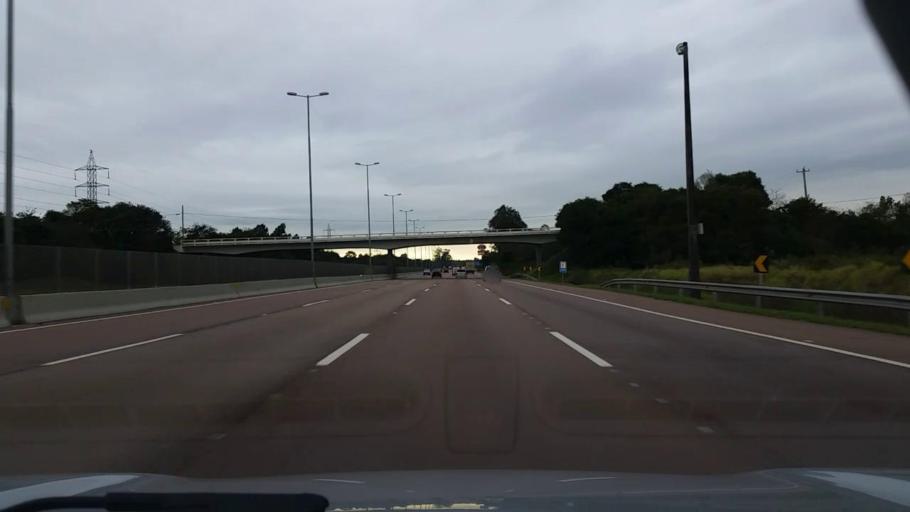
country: BR
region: Rio Grande do Sul
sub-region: Cachoeirinha
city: Cachoeirinha
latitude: -29.9538
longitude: -51.0600
